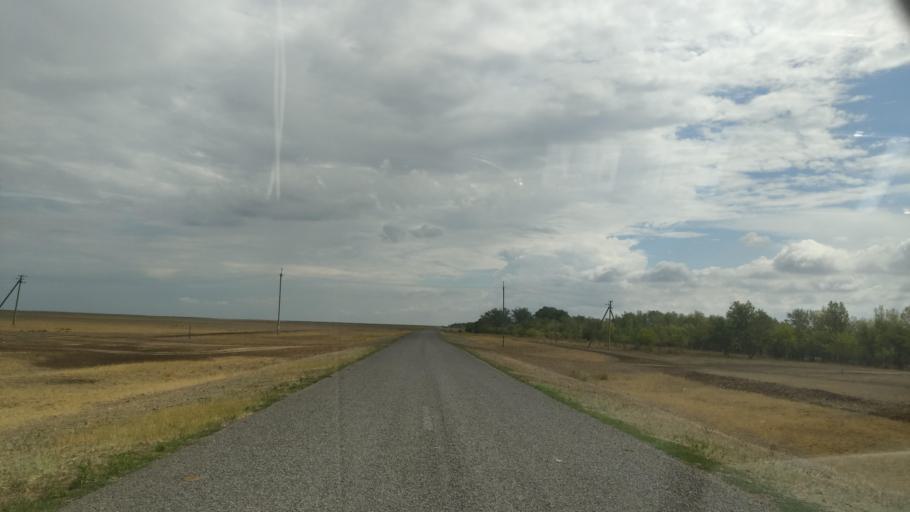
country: KZ
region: Pavlodar
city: Pavlodar
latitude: 52.6437
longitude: 77.0459
